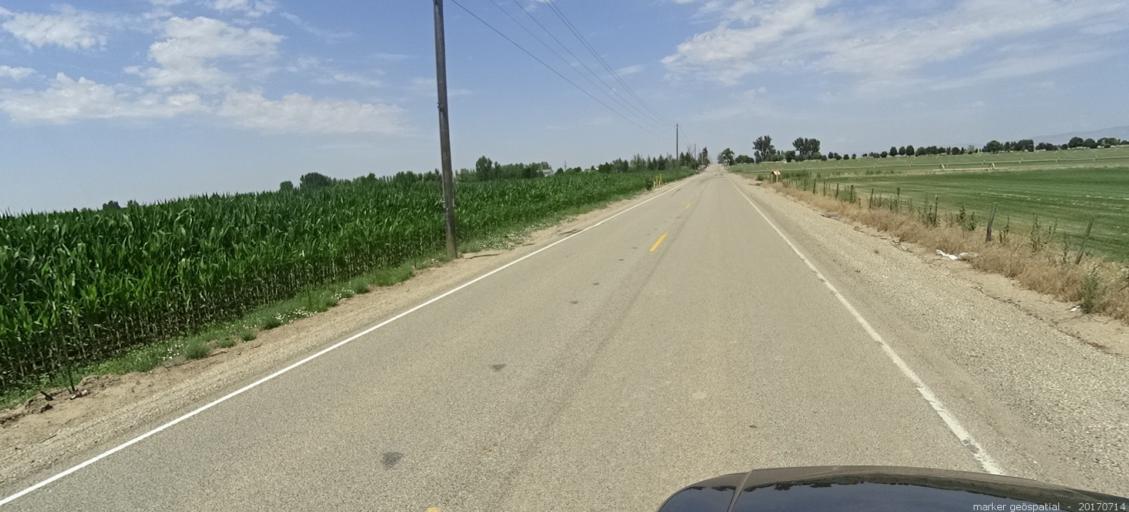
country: US
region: Idaho
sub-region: Ada County
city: Kuna
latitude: 43.5346
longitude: -116.3543
